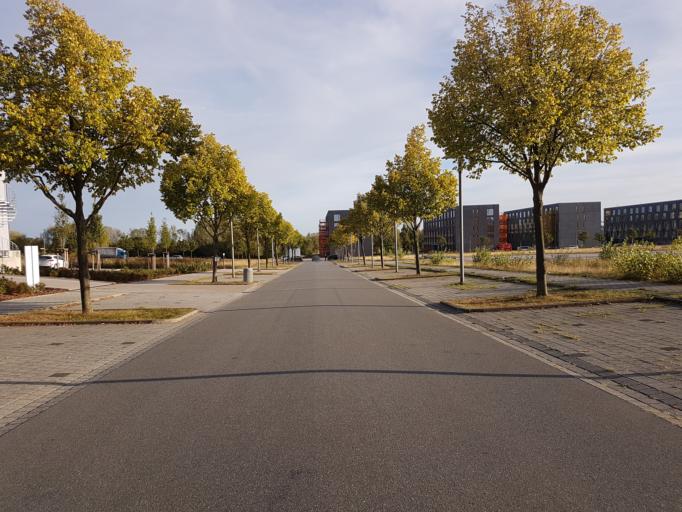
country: DE
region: Lower Saxony
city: Laatzen
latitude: 52.3155
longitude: 9.8215
